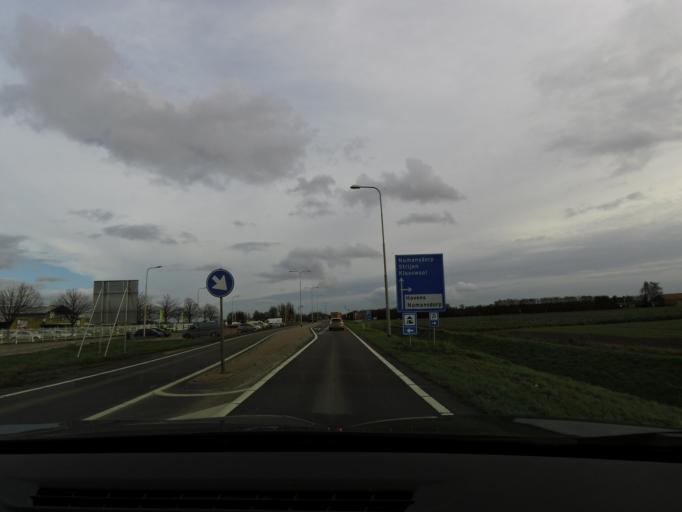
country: NL
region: North Brabant
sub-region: Gemeente Moerdijk
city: Willemstad
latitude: 51.7515
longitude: 4.4203
